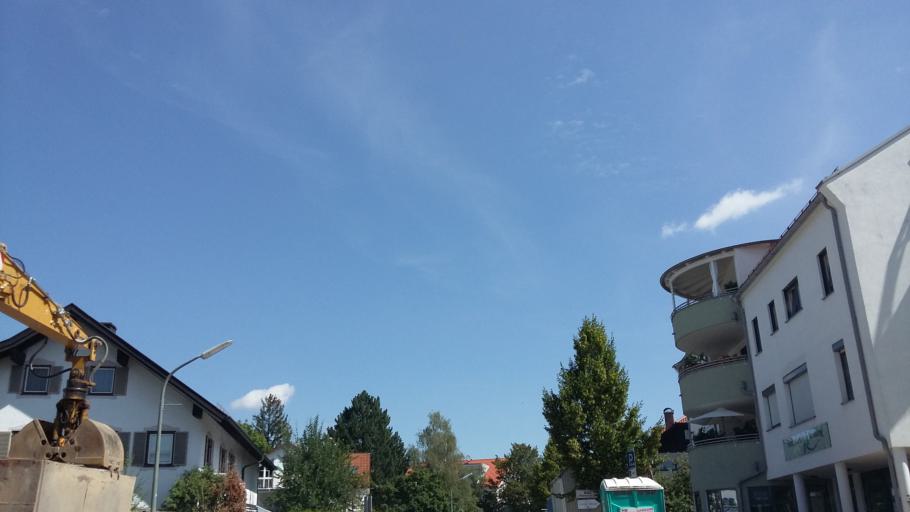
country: DE
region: Bavaria
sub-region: Upper Bavaria
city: Planegg
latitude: 48.0970
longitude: 11.4117
